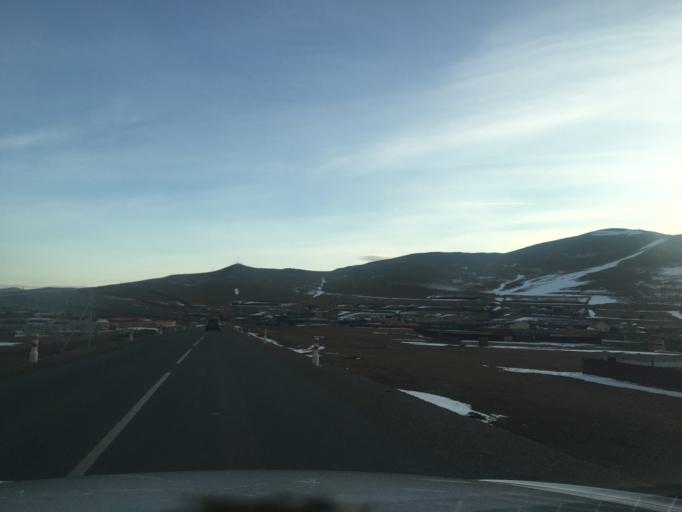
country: MN
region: Central Aimak
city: Mandal
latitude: 48.2033
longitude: 106.7063
